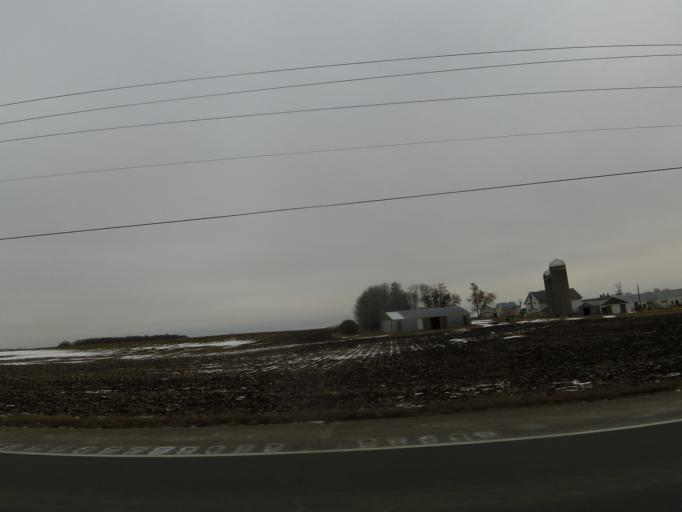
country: US
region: Minnesota
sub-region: Carver County
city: Young America (historical)
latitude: 44.7678
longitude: -93.8576
